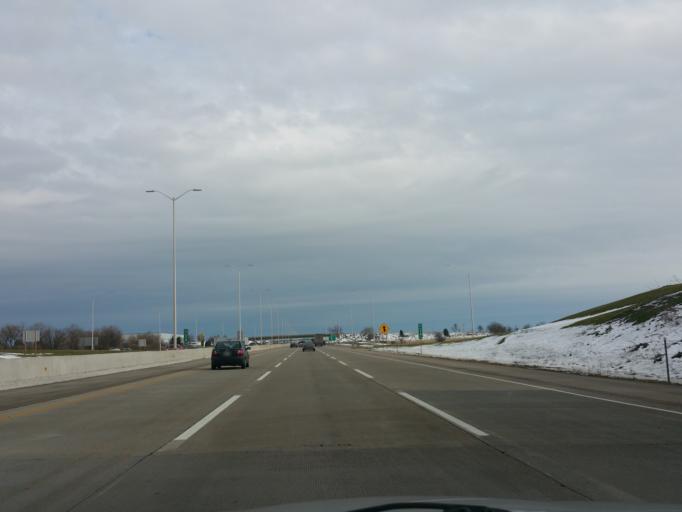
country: US
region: Illinois
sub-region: Boone County
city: Belvidere
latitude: 42.2335
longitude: -88.8345
